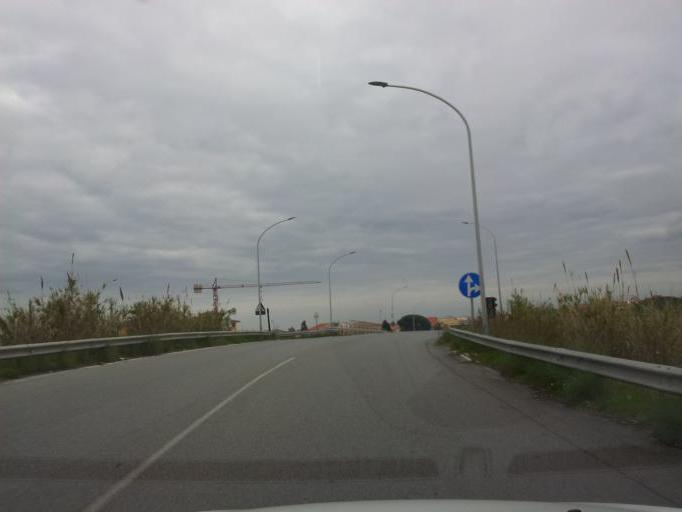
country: IT
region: Sicily
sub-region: Messina
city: Milazzo
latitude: 38.2070
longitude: 15.2371
